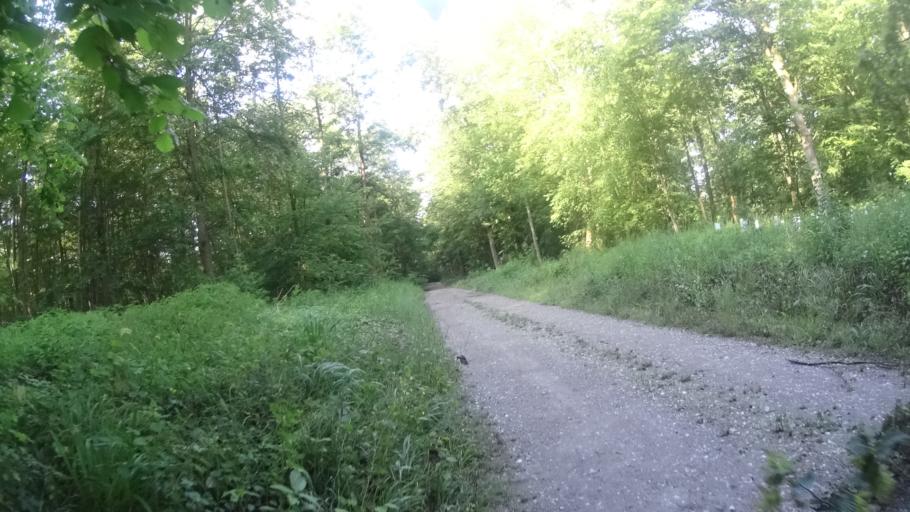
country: DE
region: Baden-Wuerttemberg
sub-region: Freiburg Region
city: Rheinau
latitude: 48.7045
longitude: 7.9585
